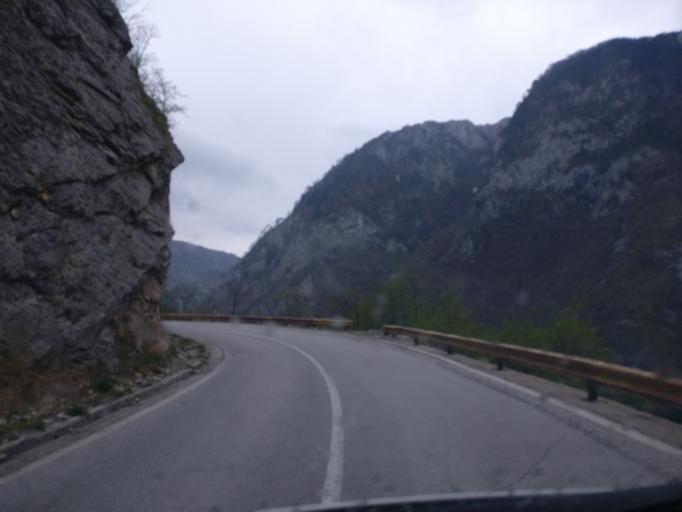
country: ME
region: Opstina Pluzine
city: Pluzine
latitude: 43.2253
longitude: 18.8458
